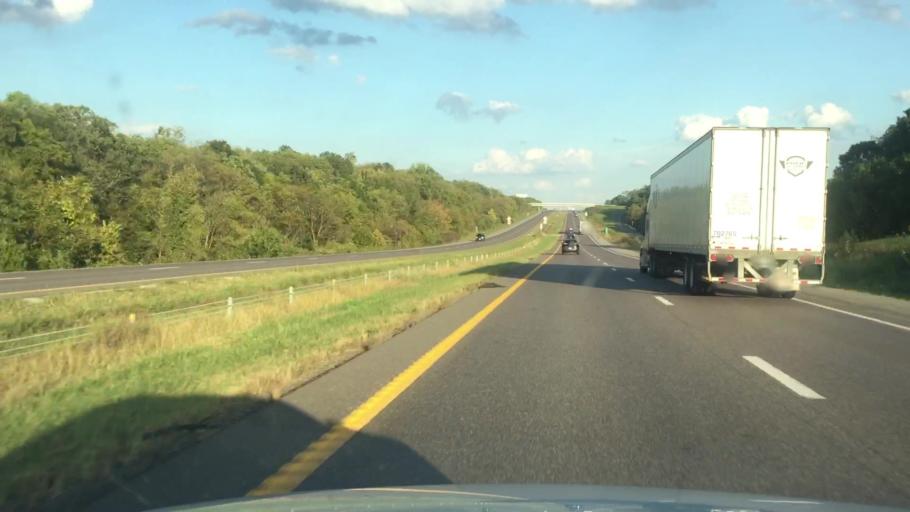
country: US
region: Missouri
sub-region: Saline County
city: Marshall
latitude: 38.9575
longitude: -93.1518
